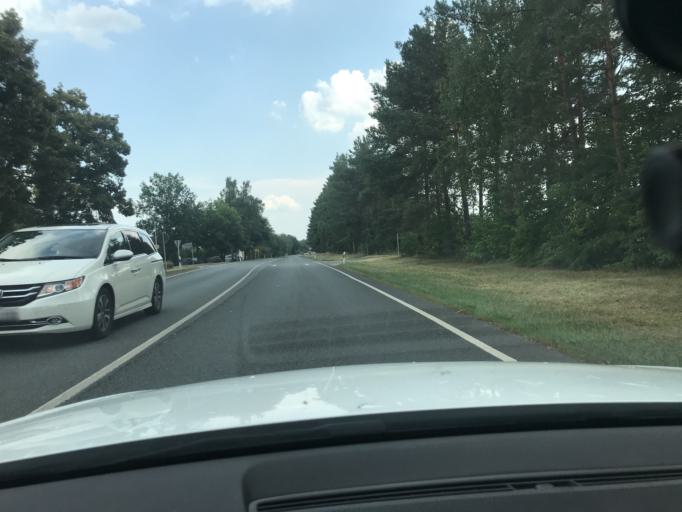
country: DE
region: Bavaria
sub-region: Upper Palatinate
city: Grafenwohr
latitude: 49.7139
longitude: 11.9188
